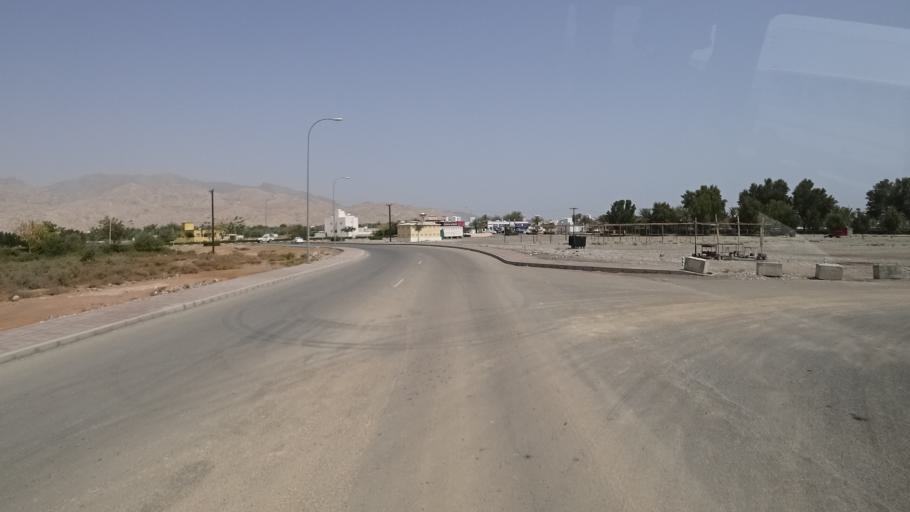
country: OM
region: Muhafazat Masqat
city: Muscat
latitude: 23.2536
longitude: 58.9105
